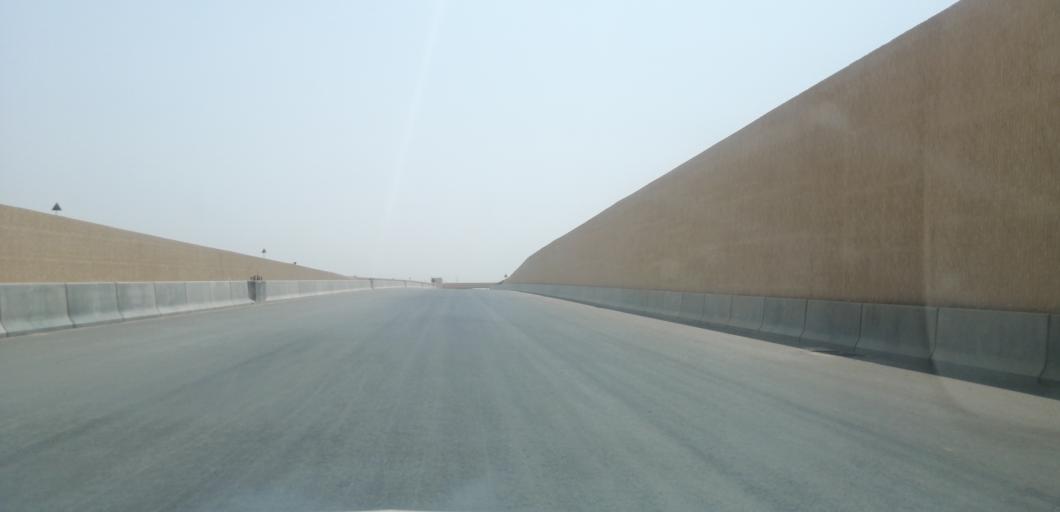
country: KW
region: Muhafazat al Jahra'
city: Al Jahra'
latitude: 29.4529
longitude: 47.5906
